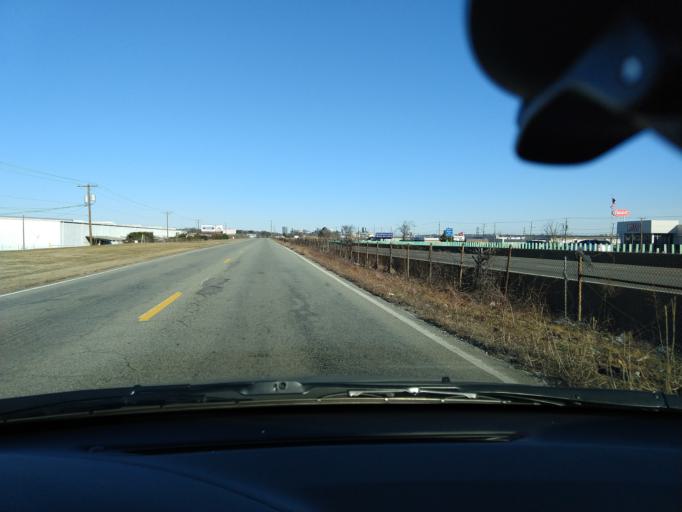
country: US
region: Virginia
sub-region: Chesterfield County
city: Bensley
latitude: 37.4842
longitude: -77.4319
